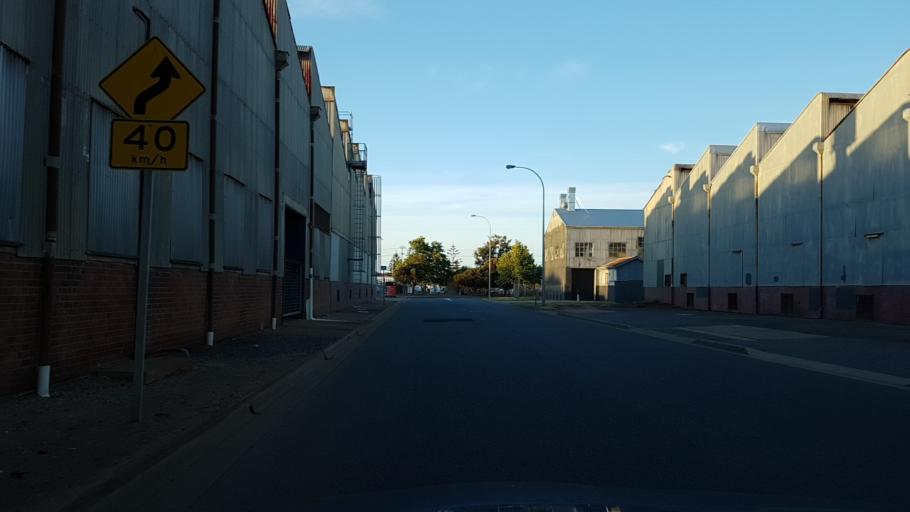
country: AU
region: South Australia
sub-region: Charles Sturt
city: Woodville North
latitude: -34.8613
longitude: 138.5378
